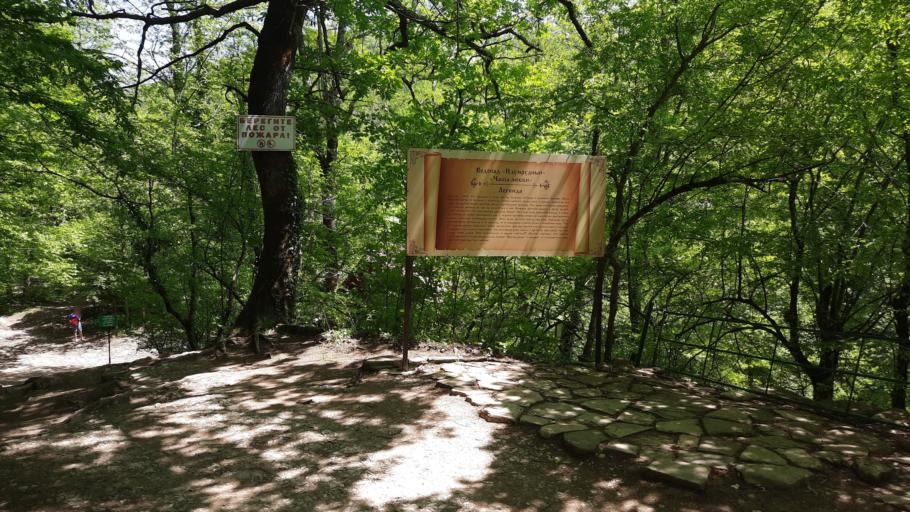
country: RU
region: Krasnodarskiy
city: Divnomorskoye
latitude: 44.5608
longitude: 38.2563
